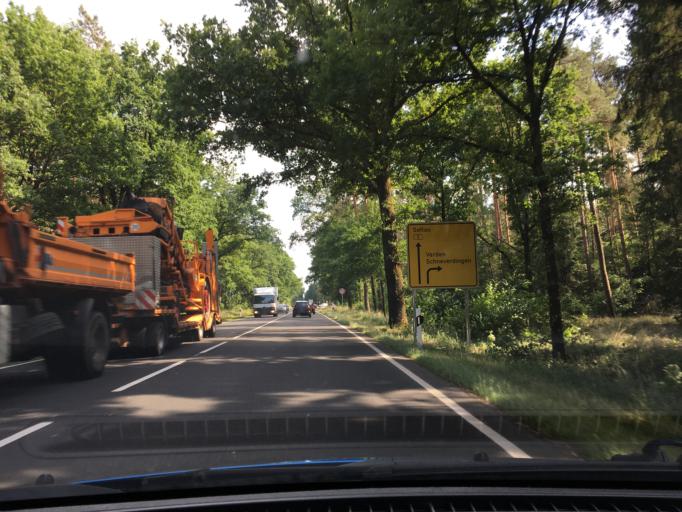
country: DE
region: Lower Saxony
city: Welle
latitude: 53.2050
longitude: 9.8234
